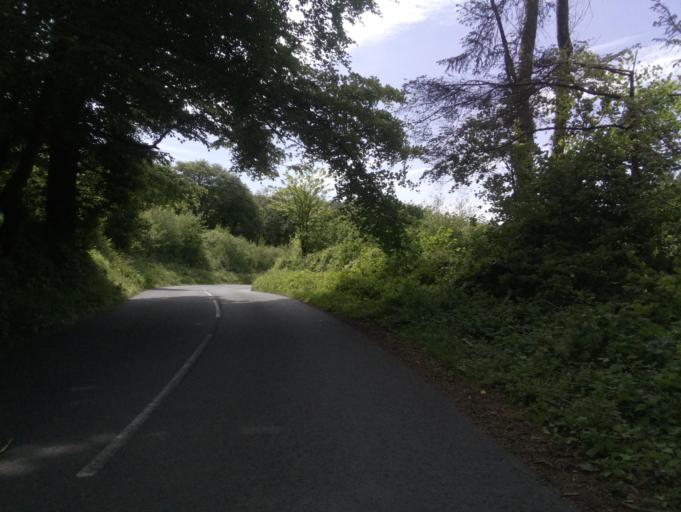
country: GB
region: England
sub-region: Devon
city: Kingsbridge
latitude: 50.3644
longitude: -3.7825
